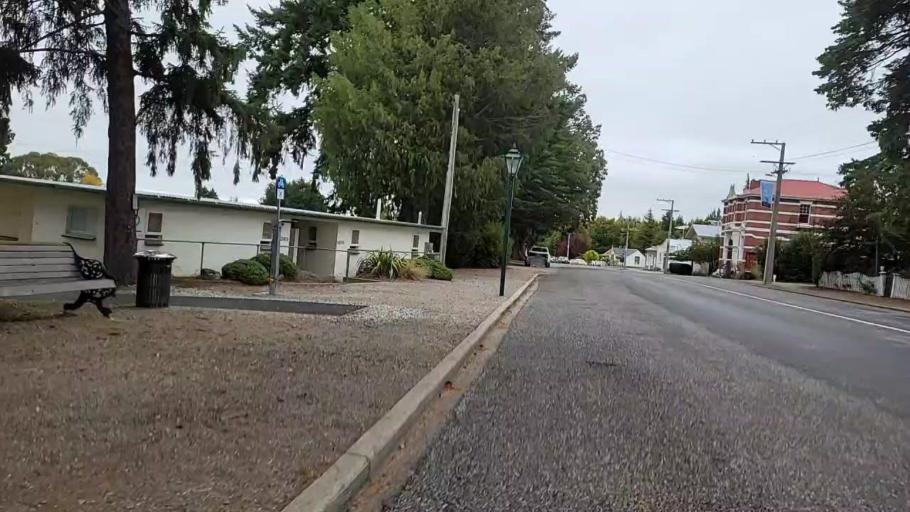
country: NZ
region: Otago
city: Oamaru
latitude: -45.0243
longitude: 170.1463
